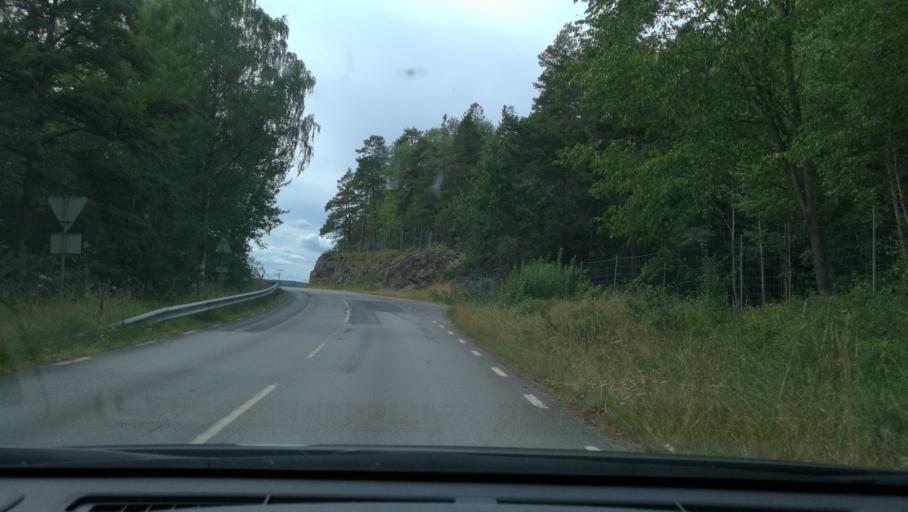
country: SE
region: OEstergoetland
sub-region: Norrkopings Kommun
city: Jursla
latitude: 58.6669
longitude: 16.2285
